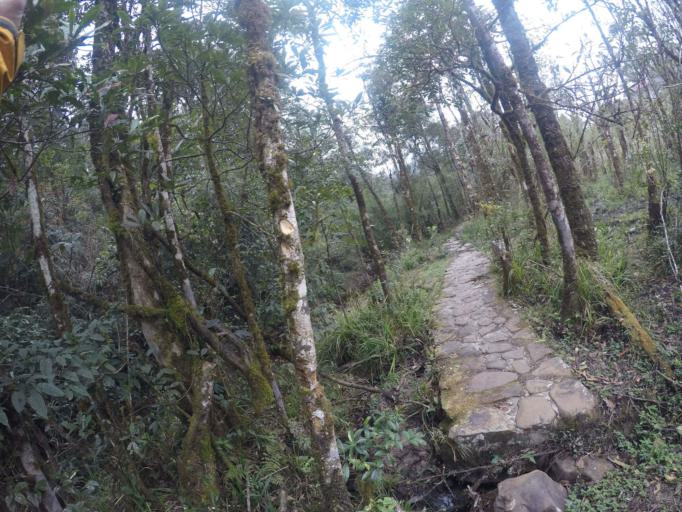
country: VN
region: Lao Cai
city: Sa Pa
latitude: 22.3493
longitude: 103.7712
